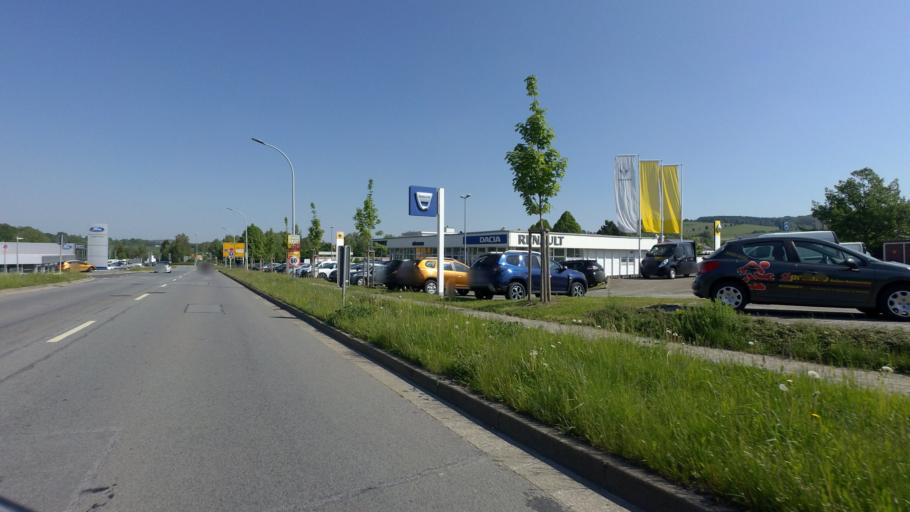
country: DE
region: Saxony
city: Neustadt in Sachsen
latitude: 51.0348
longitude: 14.2215
